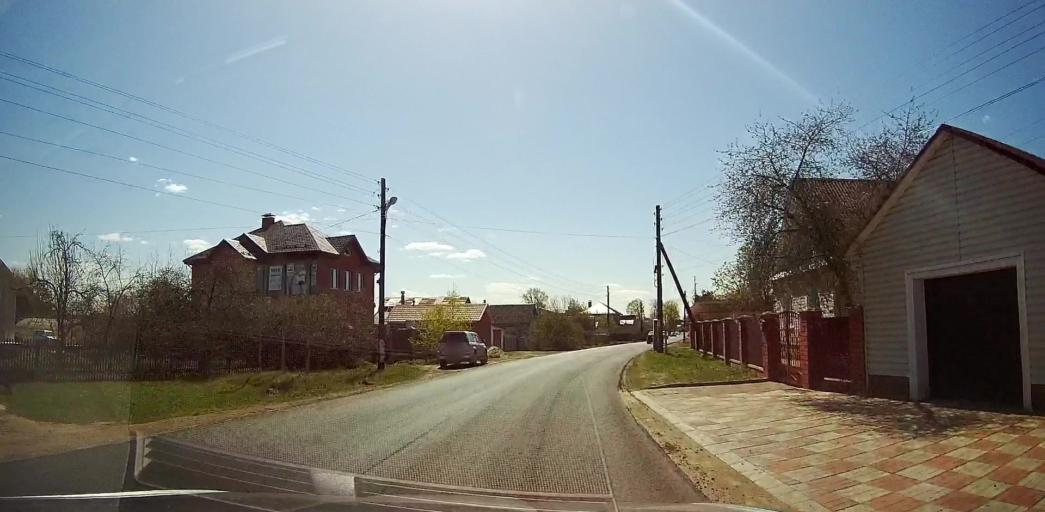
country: RU
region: Moskovskaya
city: Beloozerskiy
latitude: 55.4787
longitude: 38.3998
